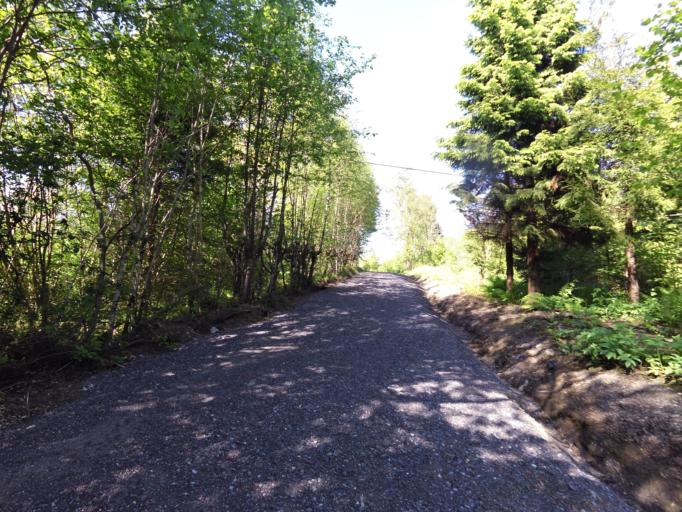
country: NO
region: Hordaland
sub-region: Stord
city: Leirvik
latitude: 59.7870
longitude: 5.4819
